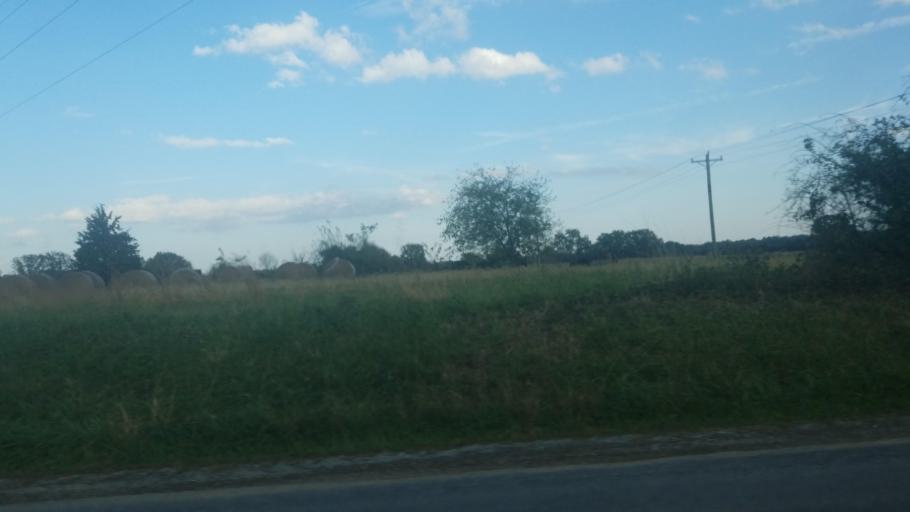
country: US
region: Illinois
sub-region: Saline County
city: Harrisburg
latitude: 37.8050
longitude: -88.6147
